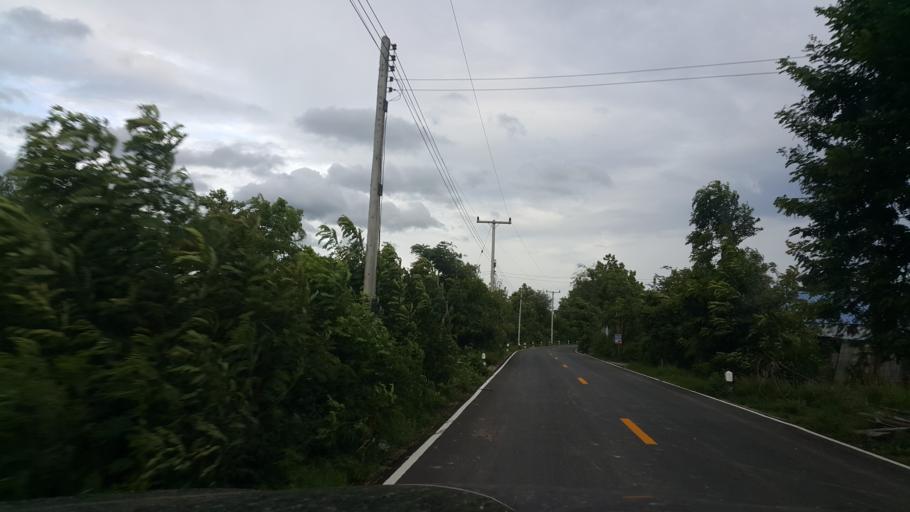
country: TH
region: Sukhothai
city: Thung Saliam
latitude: 17.1706
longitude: 99.4891
